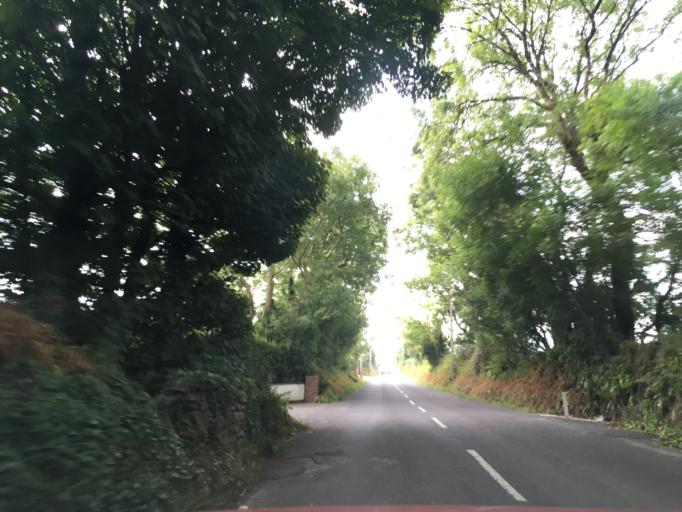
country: IE
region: Munster
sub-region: County Cork
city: Crosshaven
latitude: 51.7941
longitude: -8.2982
